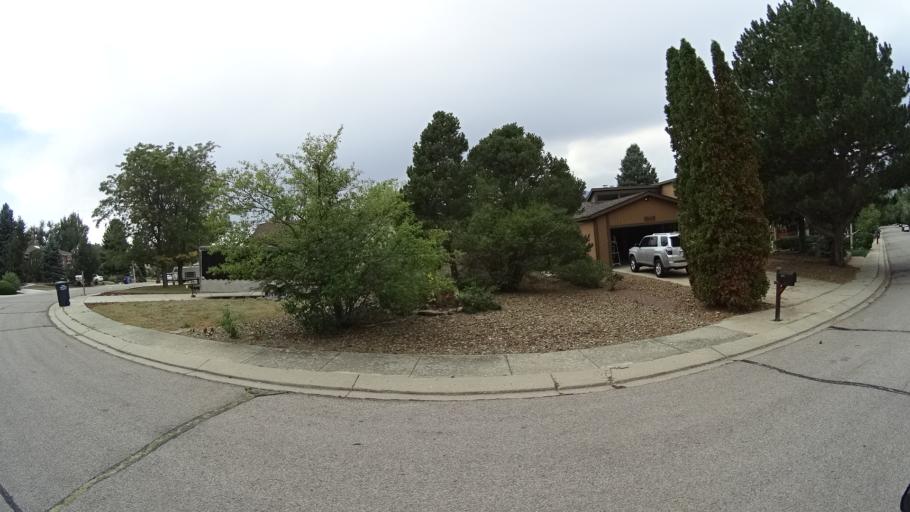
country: US
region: Colorado
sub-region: El Paso County
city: Colorado Springs
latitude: 38.8717
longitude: -104.7862
